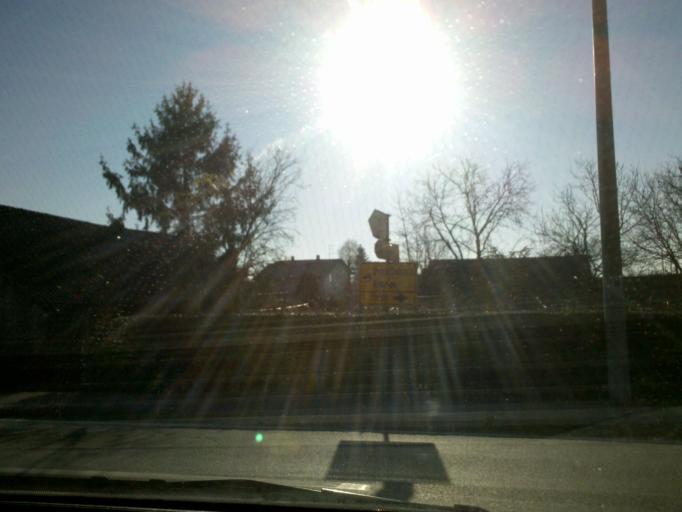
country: HR
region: Medimurska
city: Gorican
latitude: 46.3461
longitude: 16.6761
